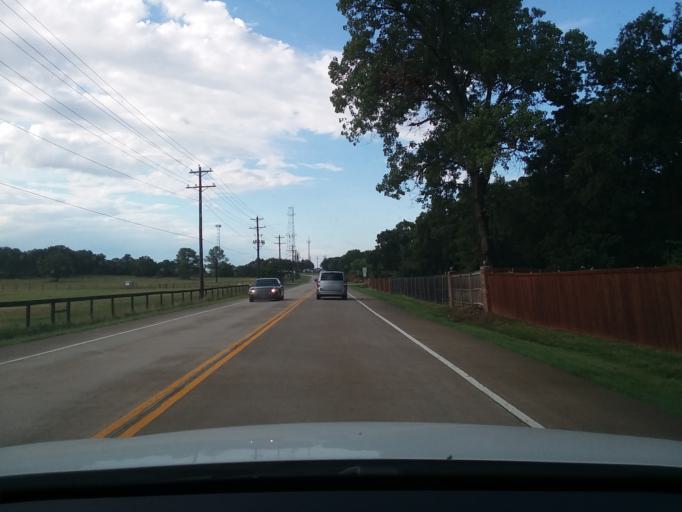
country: US
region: Texas
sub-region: Denton County
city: Copper Canyon
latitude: 33.0839
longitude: -97.1100
